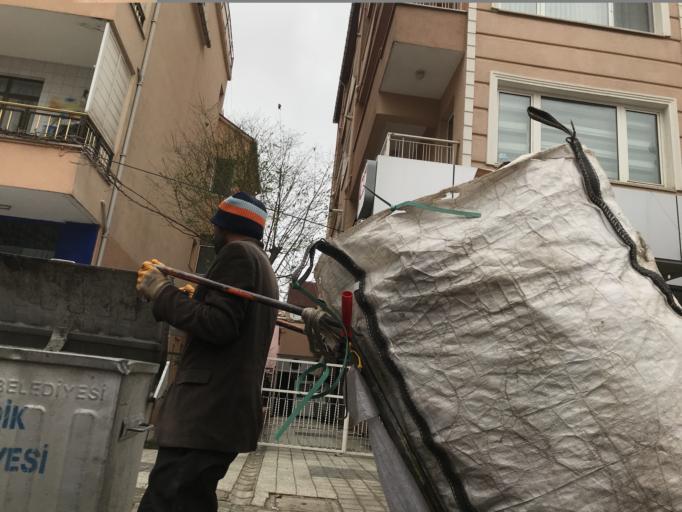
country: TR
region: Istanbul
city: Pendik
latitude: 40.8838
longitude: 29.2285
